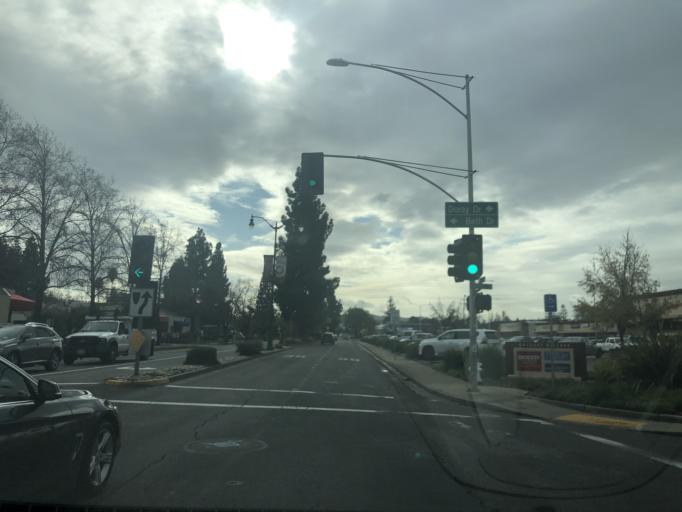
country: US
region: California
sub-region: Contra Costa County
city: Pleasant Hill
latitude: 37.9549
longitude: -122.0602
